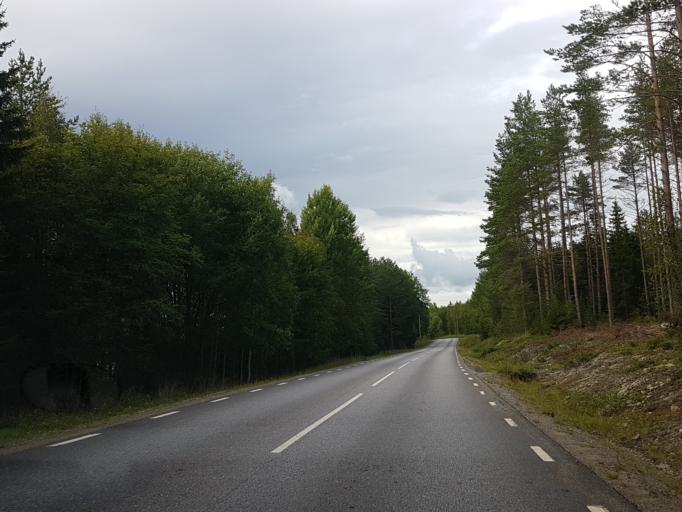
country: SE
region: Vaesterbotten
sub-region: Umea Kommun
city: Holmsund
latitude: 63.7727
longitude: 20.3873
